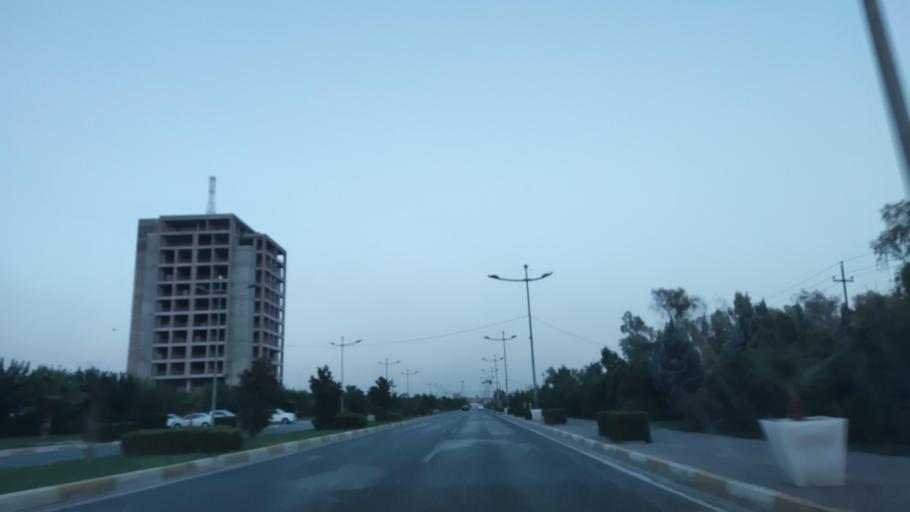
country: IQ
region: Arbil
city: Erbil
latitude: 36.1985
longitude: 43.9845
